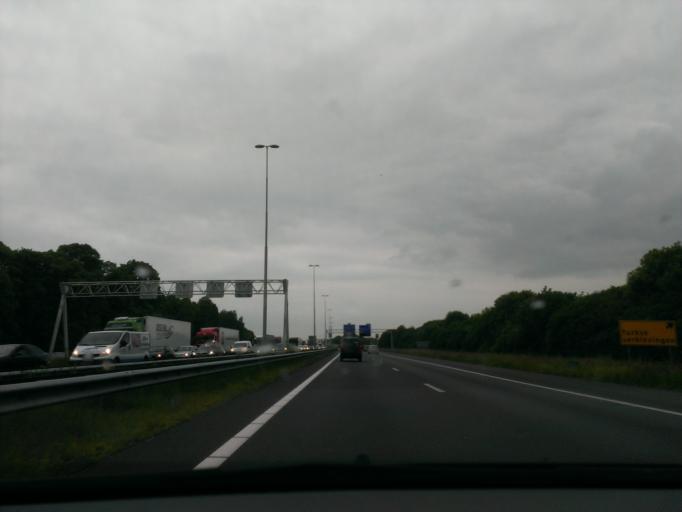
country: NL
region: Gelderland
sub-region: Gemeente Lochem
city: Epse
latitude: 52.2378
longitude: 6.2265
